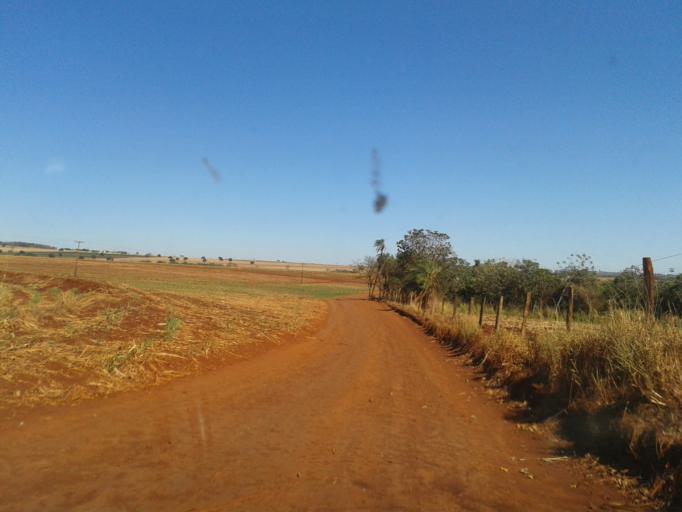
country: BR
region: Minas Gerais
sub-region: Centralina
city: Centralina
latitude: -18.5908
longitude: -49.1652
